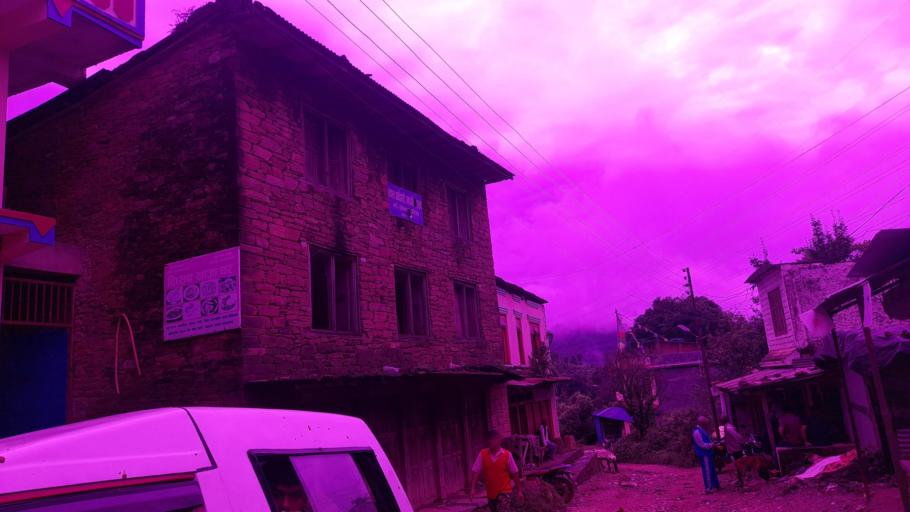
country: NP
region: Central Region
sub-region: Bagmati Zone
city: Kathmandu
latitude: 27.8637
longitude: 85.2205
